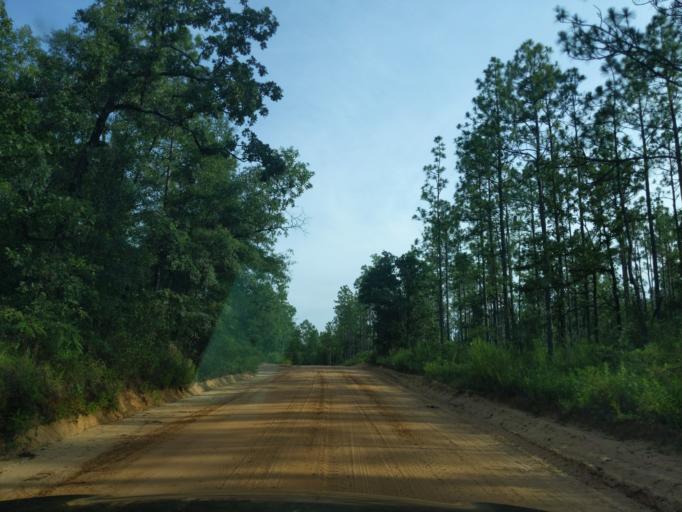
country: US
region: Florida
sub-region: Gadsden County
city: Midway
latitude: 30.3930
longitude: -84.4097
